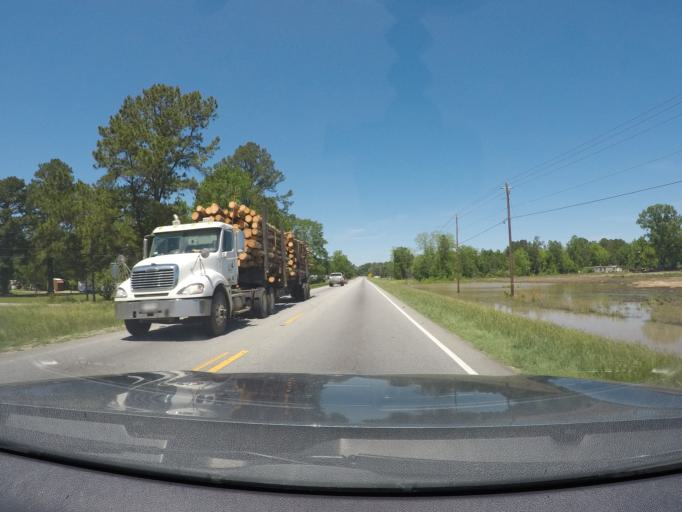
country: US
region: Georgia
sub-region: Chatham County
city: Bloomingdale
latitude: 32.1860
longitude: -81.4014
